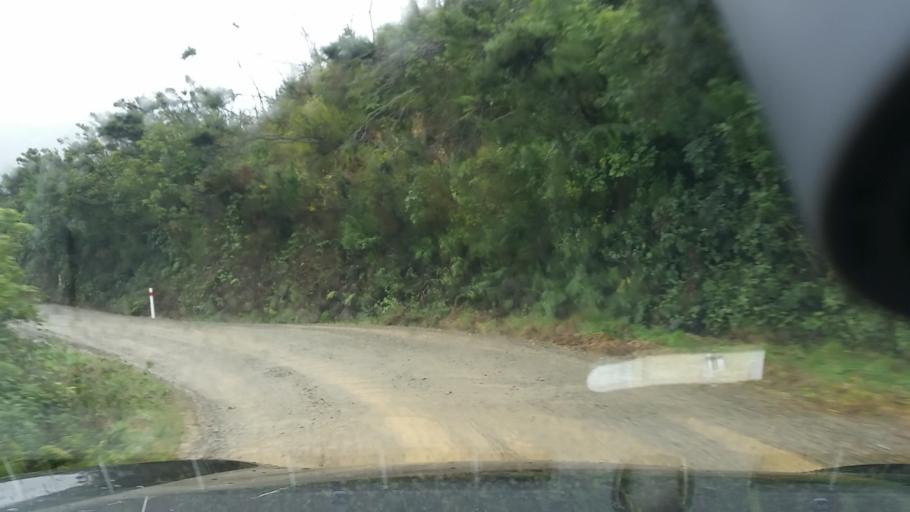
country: NZ
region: Marlborough
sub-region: Marlborough District
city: Picton
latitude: -41.3455
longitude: 174.0755
